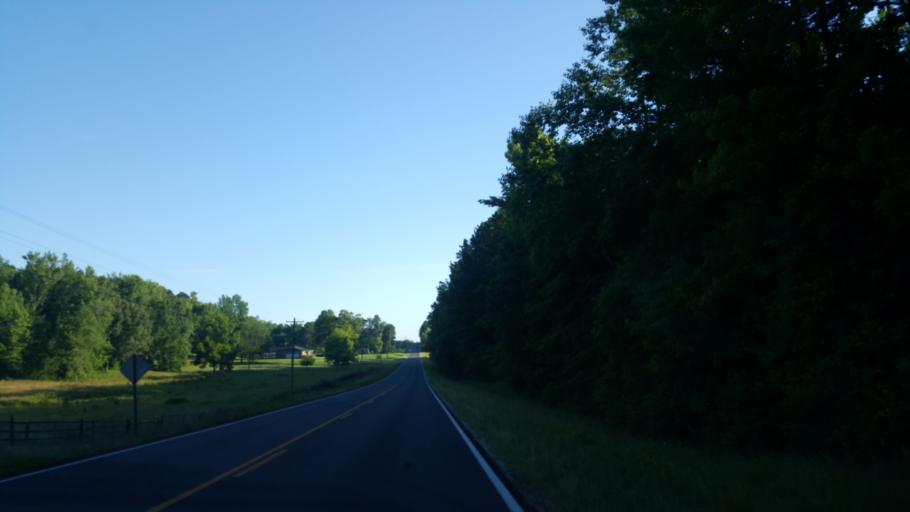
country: US
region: Tennessee
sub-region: Henderson County
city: Lexington
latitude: 35.5543
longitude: -88.3853
